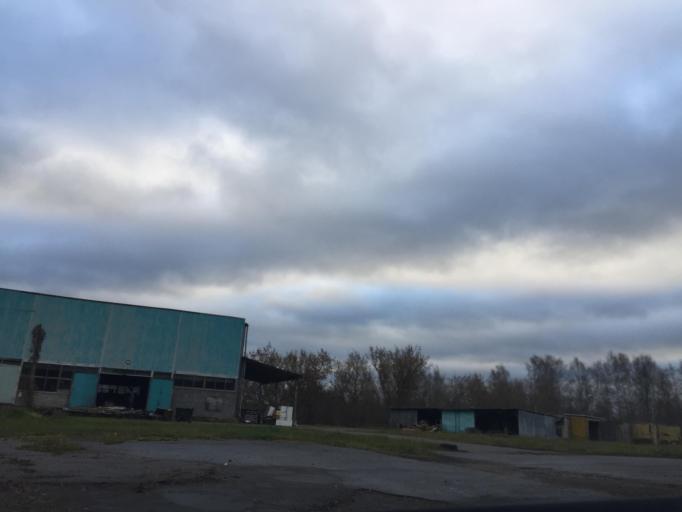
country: LV
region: Jurmala
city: Jurmala
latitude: 56.9557
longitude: 23.7750
